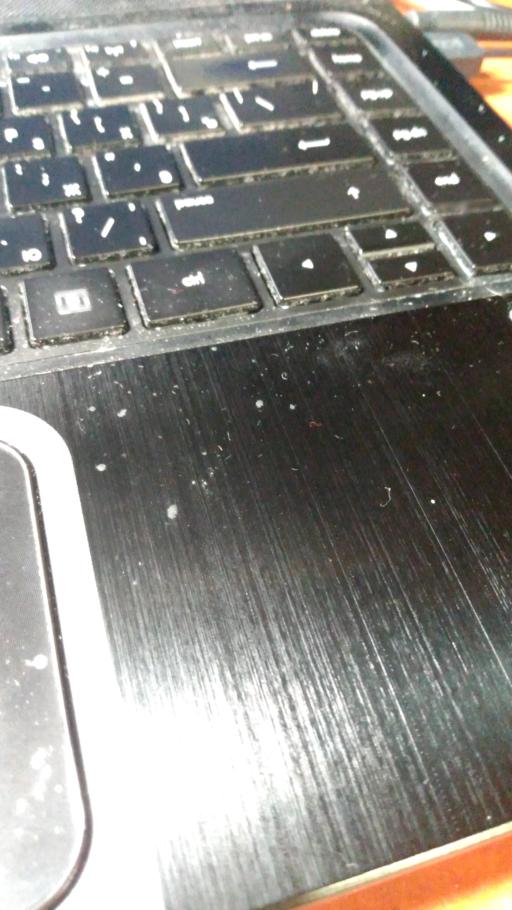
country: RU
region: Tverskaya
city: Vyshniy Volochek
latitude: 57.6689
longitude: 34.6728
